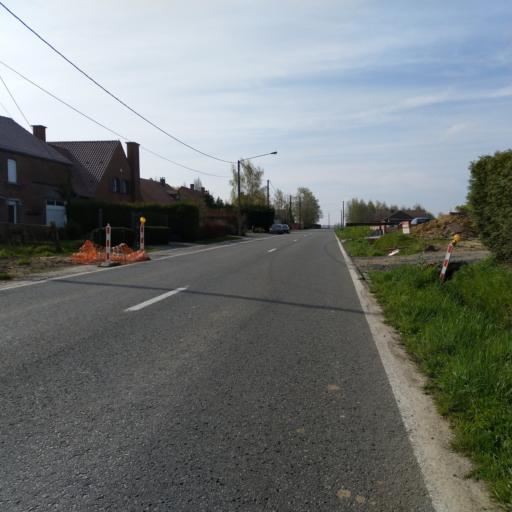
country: BE
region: Wallonia
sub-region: Province du Hainaut
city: Quevy-le-Petit
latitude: 50.3564
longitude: 3.8893
